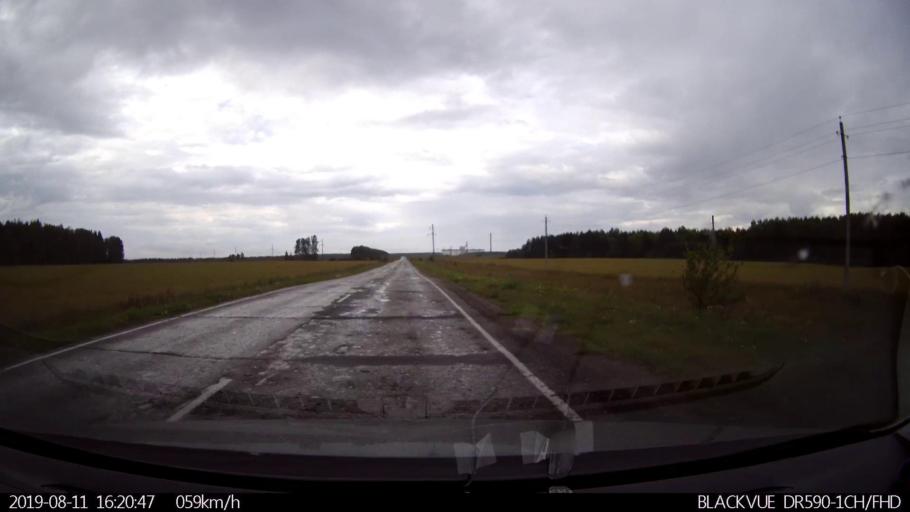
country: RU
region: Ulyanovsk
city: Mayna
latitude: 54.0746
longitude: 47.6012
